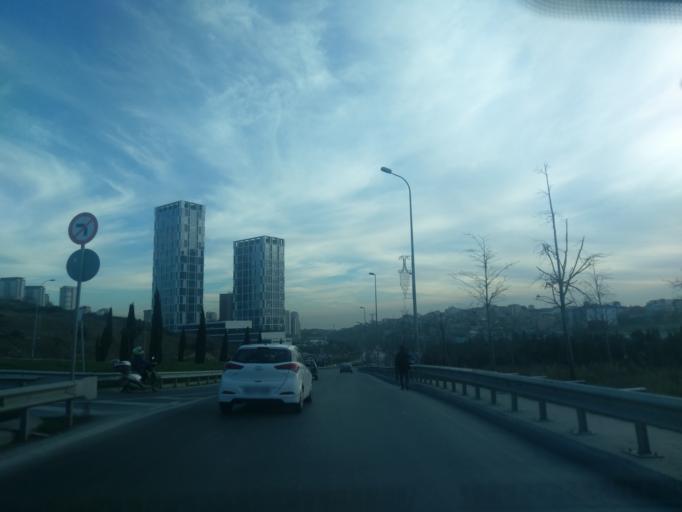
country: TR
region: Istanbul
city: Basaksehir
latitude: 41.0605
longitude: 28.7588
